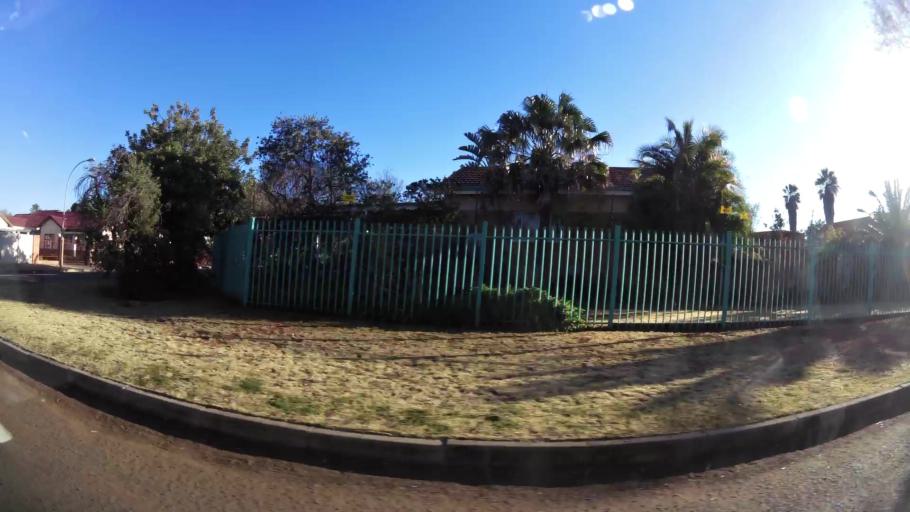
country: ZA
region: Northern Cape
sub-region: Frances Baard District Municipality
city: Kimberley
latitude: -28.7480
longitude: 24.7256
